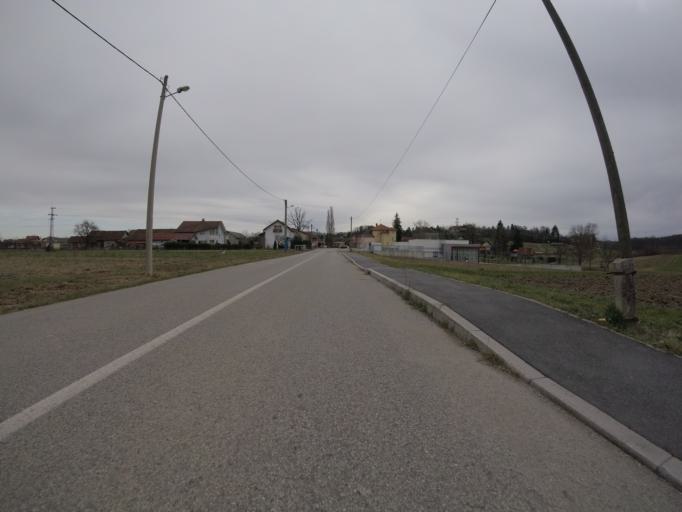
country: HR
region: Grad Zagreb
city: Strmec
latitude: 45.6639
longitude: 15.9409
